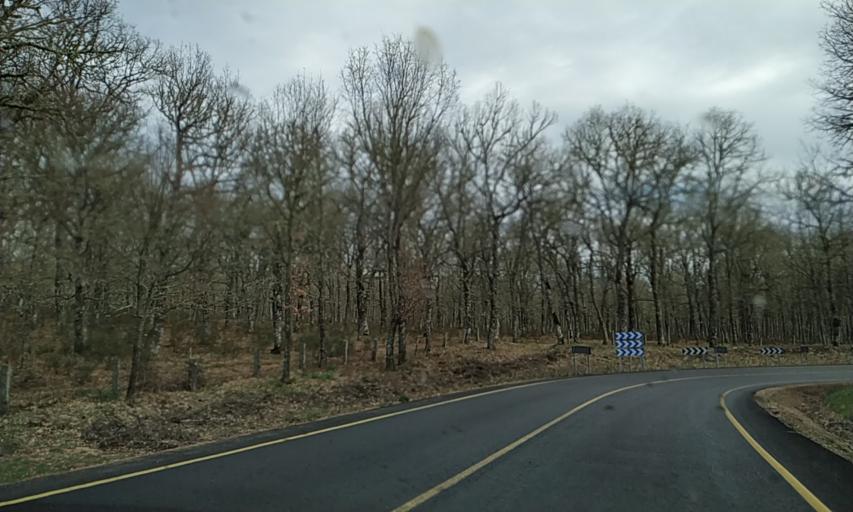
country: ES
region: Castille and Leon
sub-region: Provincia de Salamanca
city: Villasrubias
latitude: 40.3248
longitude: -6.6444
